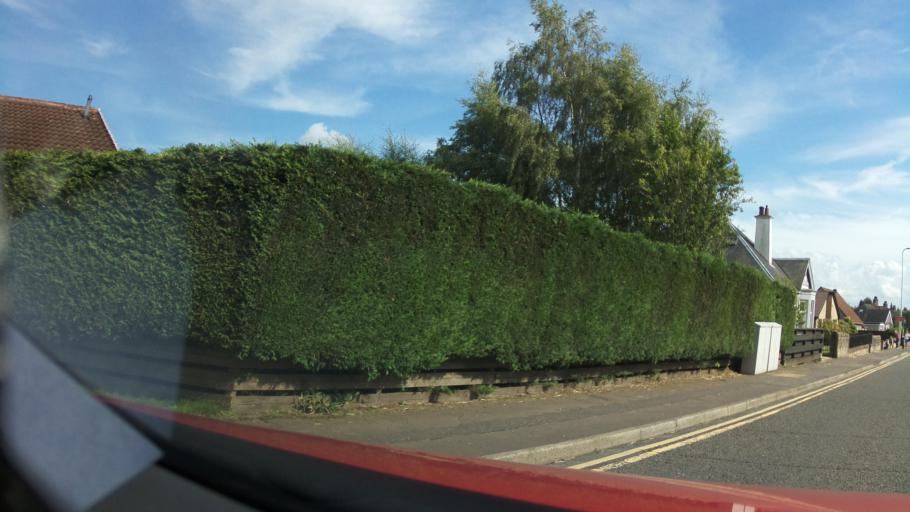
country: GB
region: Scotland
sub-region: Falkirk
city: Larbert
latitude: 56.0258
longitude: -3.8398
